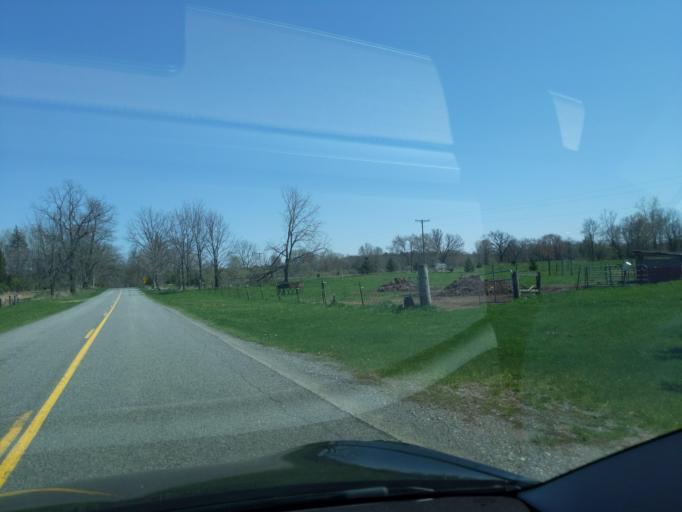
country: US
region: Michigan
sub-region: Ingham County
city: Stockbridge
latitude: 42.4881
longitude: -84.1848
